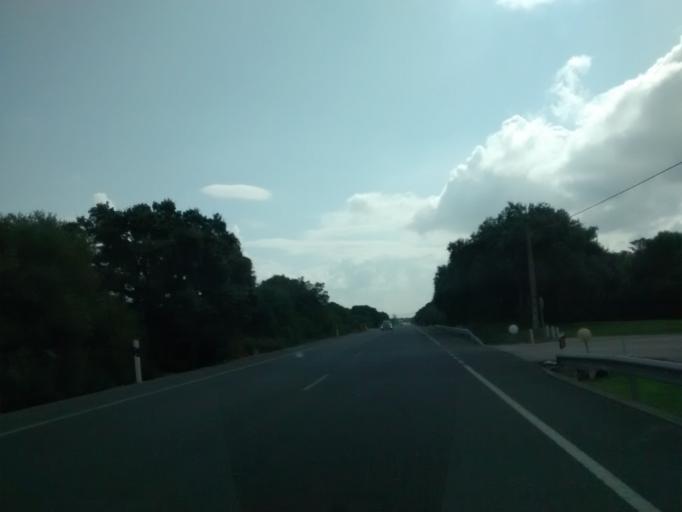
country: ES
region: Andalusia
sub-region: Provincia de Cadiz
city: Barbate de Franco
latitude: 36.2462
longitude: -5.9041
